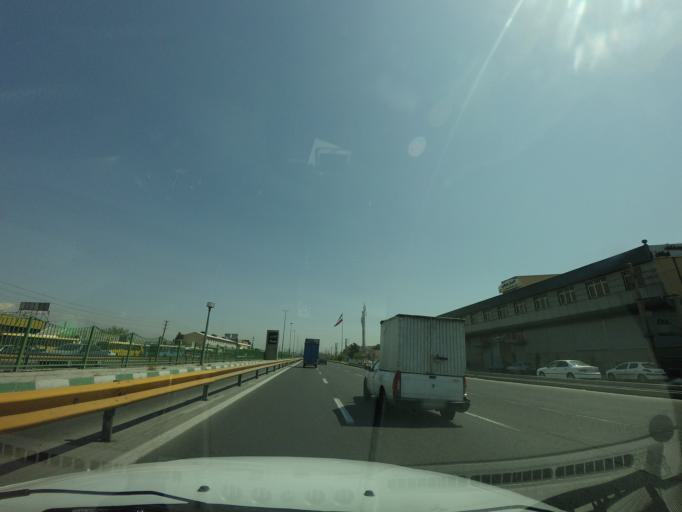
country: IR
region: Tehran
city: Tehran
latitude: 35.6284
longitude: 51.3363
